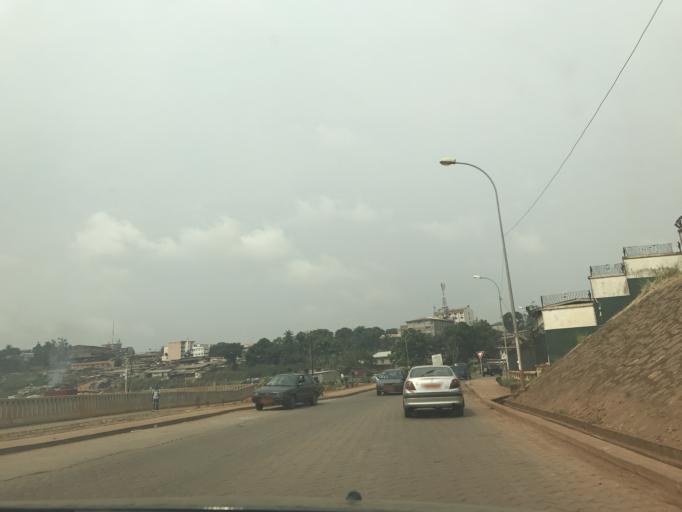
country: CM
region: Centre
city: Yaounde
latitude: 3.8303
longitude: 11.5135
